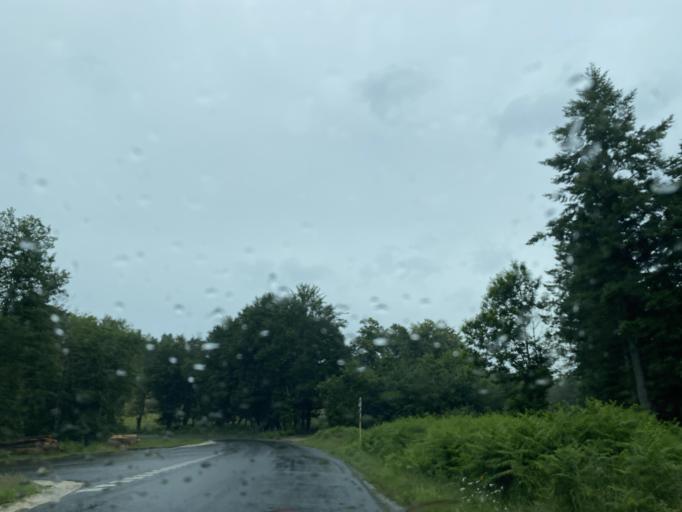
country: FR
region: Auvergne
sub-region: Departement du Puy-de-Dome
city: Celles-sur-Durolle
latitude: 45.8957
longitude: 3.6372
